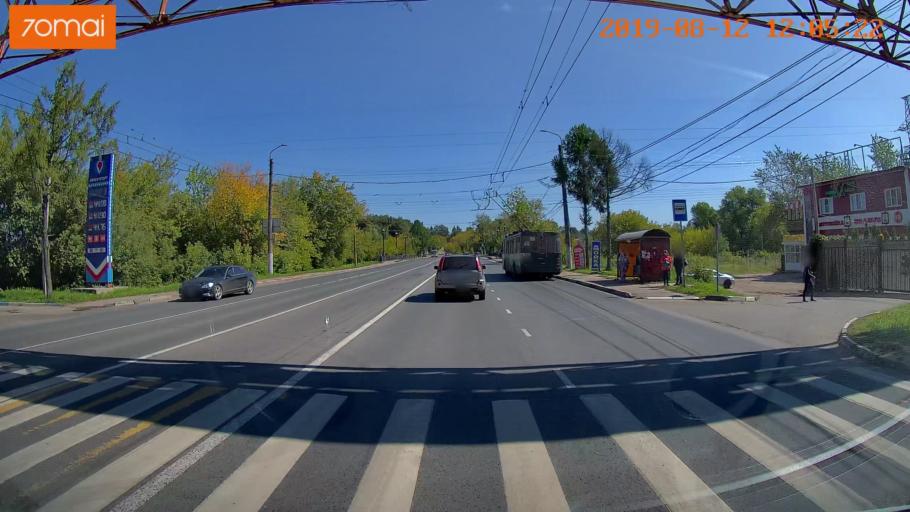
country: RU
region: Ivanovo
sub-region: Gorod Ivanovo
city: Ivanovo
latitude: 56.9938
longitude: 41.0140
